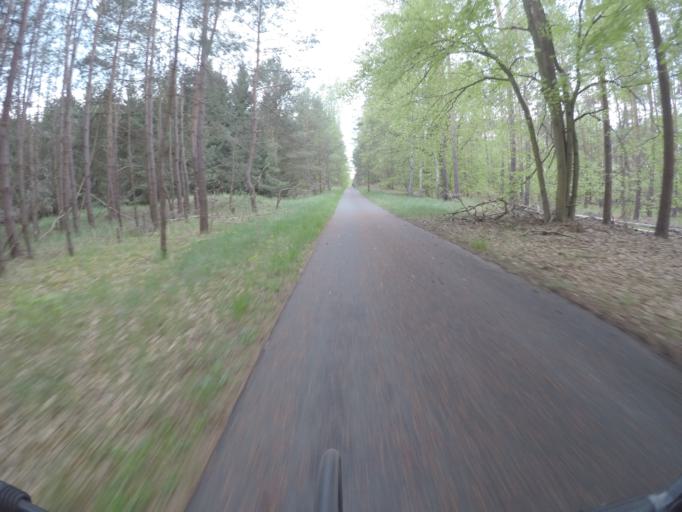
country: DE
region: Brandenburg
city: Biesenthal
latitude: 52.8105
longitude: 13.6337
